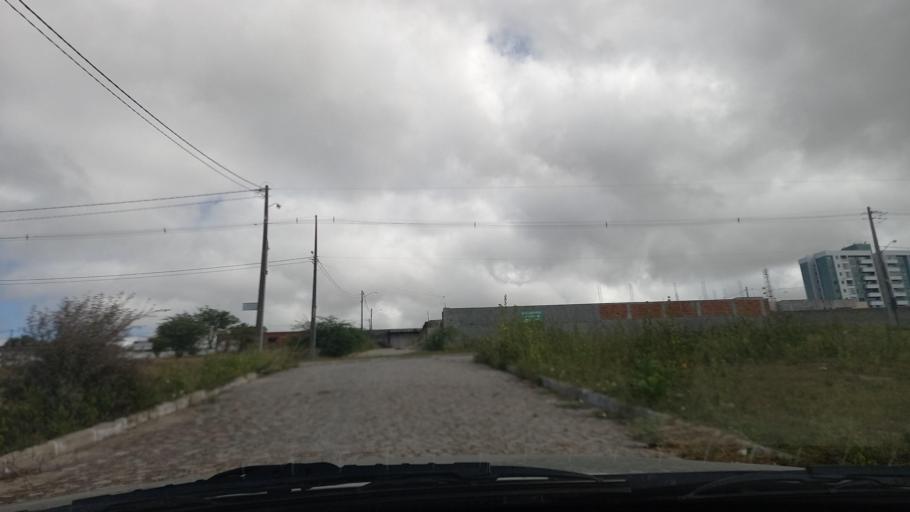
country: BR
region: Pernambuco
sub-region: Caruaru
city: Caruaru
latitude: -8.3043
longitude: -35.9601
